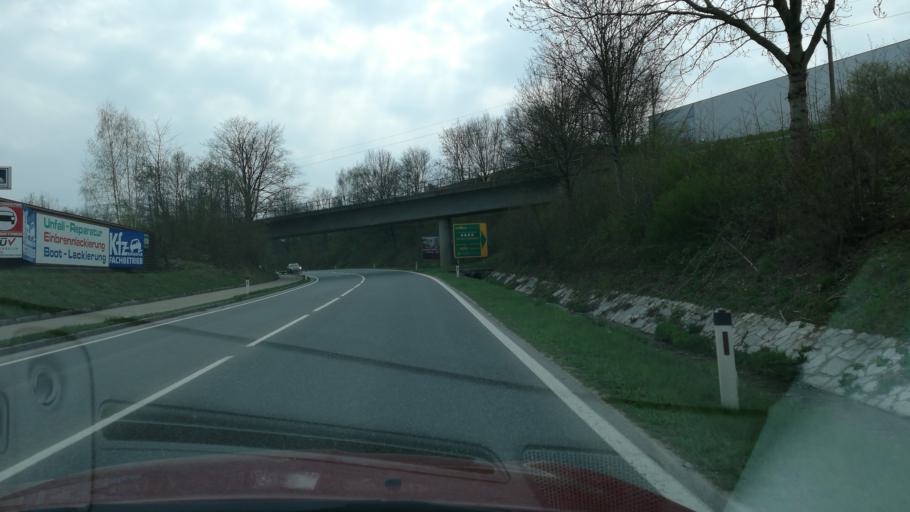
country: AT
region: Upper Austria
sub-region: Politischer Bezirk Vocklabruck
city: Lenzing
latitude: 47.9558
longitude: 13.6063
